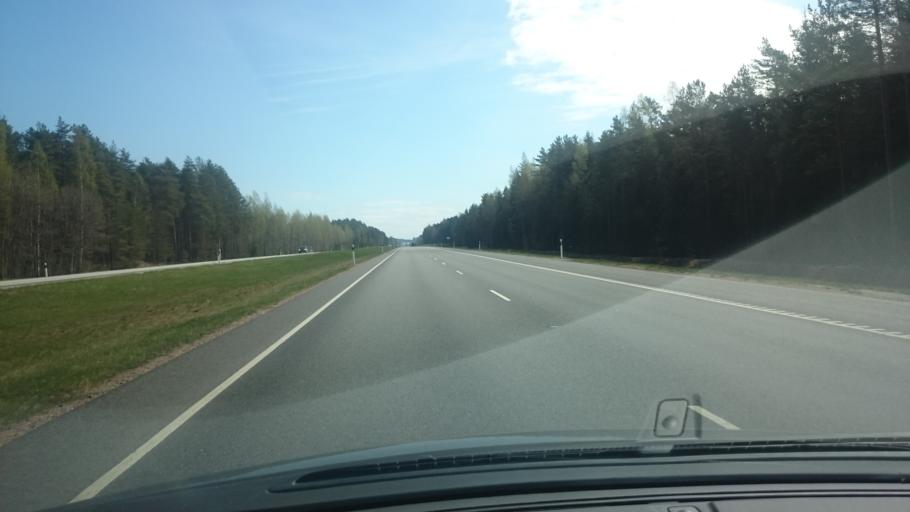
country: EE
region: Harju
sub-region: Loksa linn
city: Loksa
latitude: 59.4624
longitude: 25.6463
